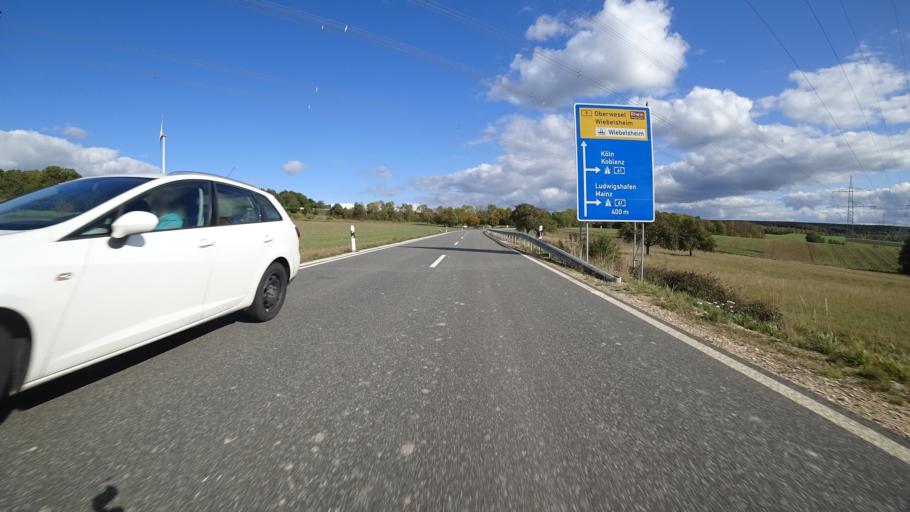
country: DE
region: Rheinland-Pfalz
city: Wiebelsheim
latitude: 50.0776
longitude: 7.6139
